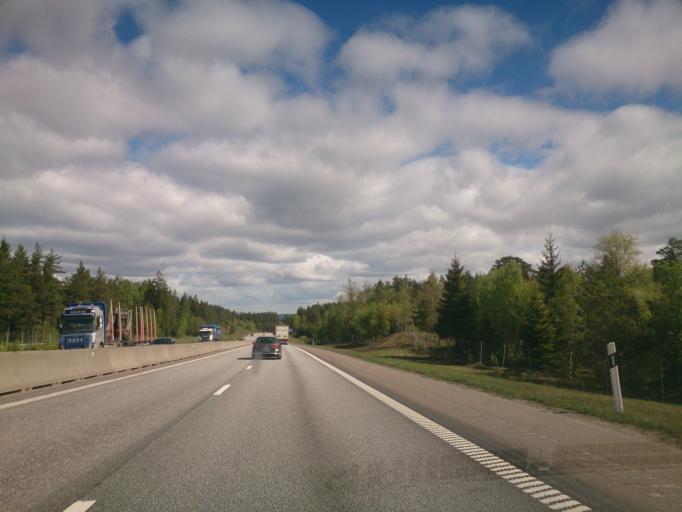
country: SE
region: OEstergoetland
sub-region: Norrkopings Kommun
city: Kimstad
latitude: 58.5389
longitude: 16.0409
